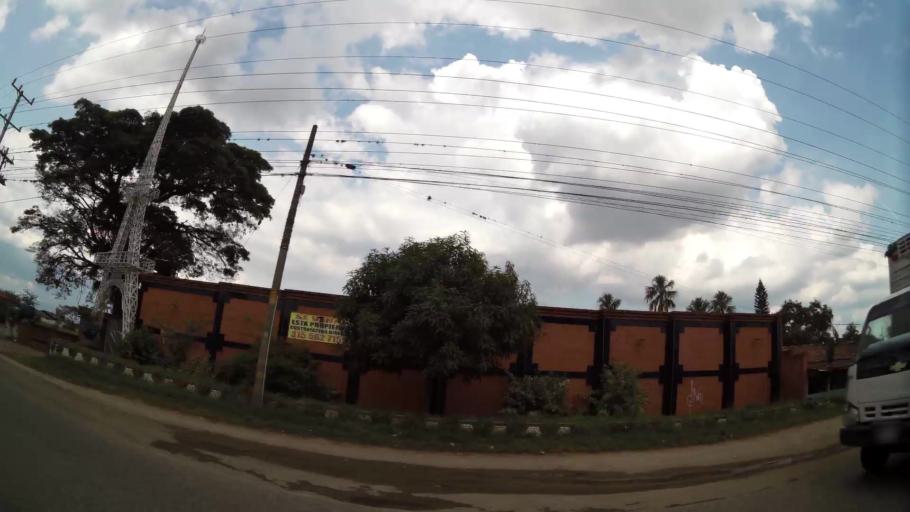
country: CO
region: Valle del Cauca
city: Cali
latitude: 3.4461
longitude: -76.4639
